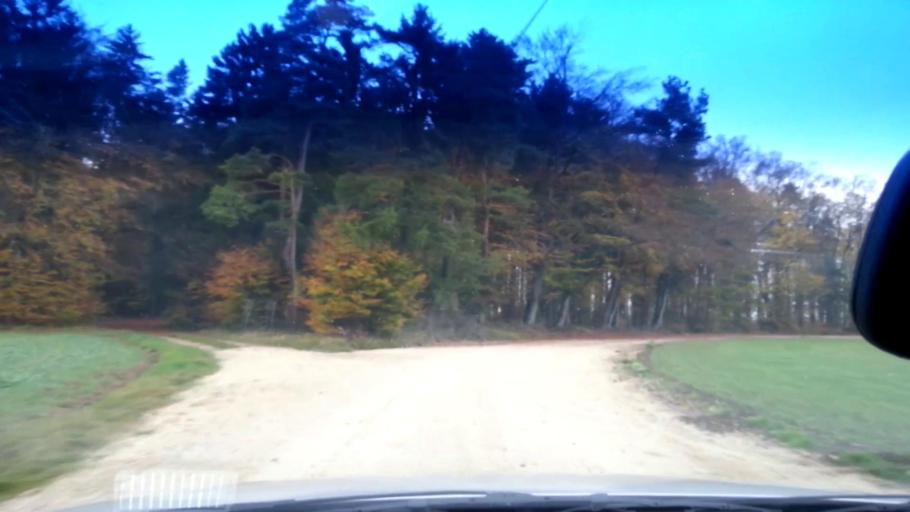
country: DE
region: Bavaria
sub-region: Upper Franconia
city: Wattendorf
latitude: 50.0111
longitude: 11.1471
